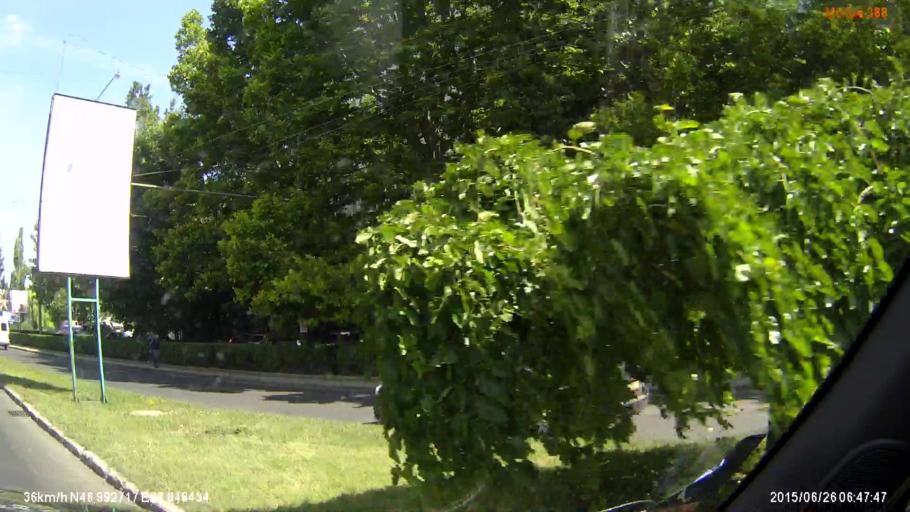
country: MD
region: Chisinau
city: Chisinau
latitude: 46.9927
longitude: 28.8485
